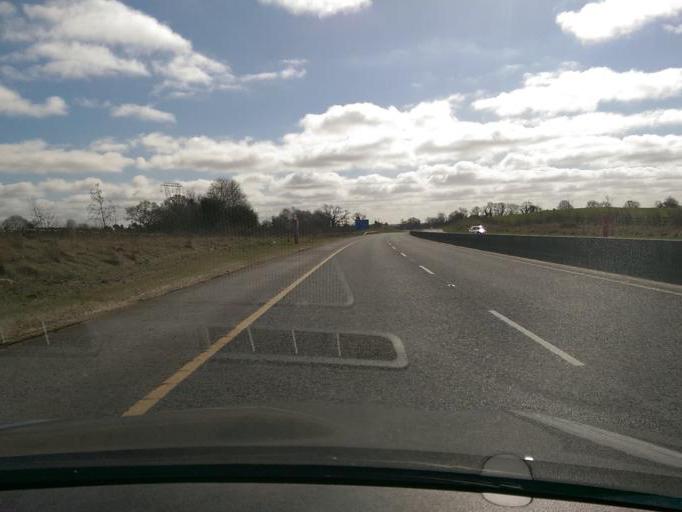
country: IE
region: Leinster
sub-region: An Iarmhi
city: Kilbeggan
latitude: 53.3690
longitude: -7.5336
